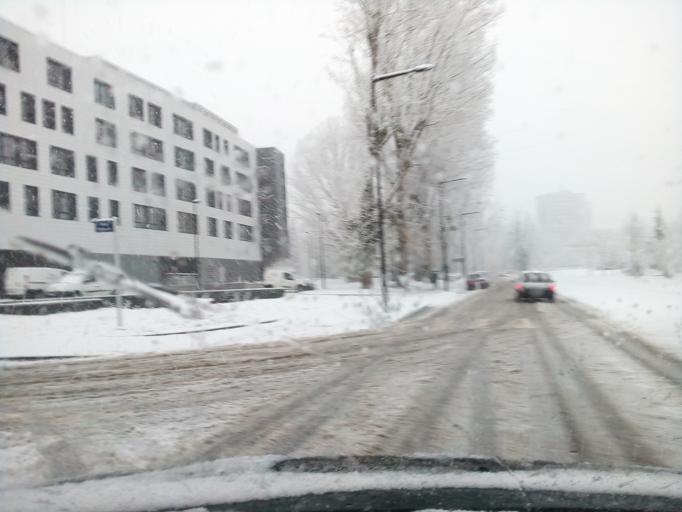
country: FR
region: Rhone-Alpes
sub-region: Departement de l'Isere
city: Saint-Martin-d'Heres
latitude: 45.1899
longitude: 5.7661
